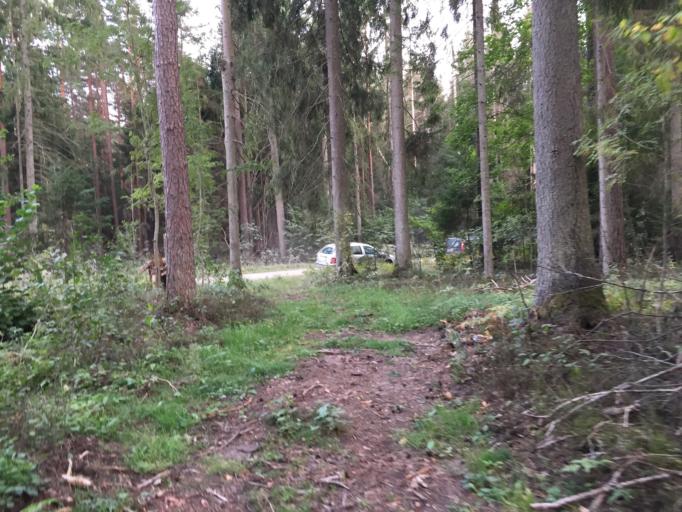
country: LV
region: Baldone
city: Baldone
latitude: 56.7547
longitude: 24.4066
